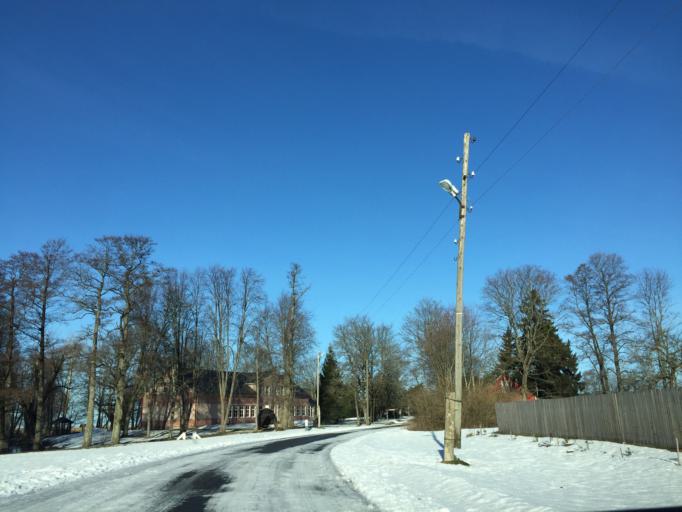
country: LV
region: Salacgrivas
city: Ainazi
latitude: 58.0796
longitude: 24.4912
